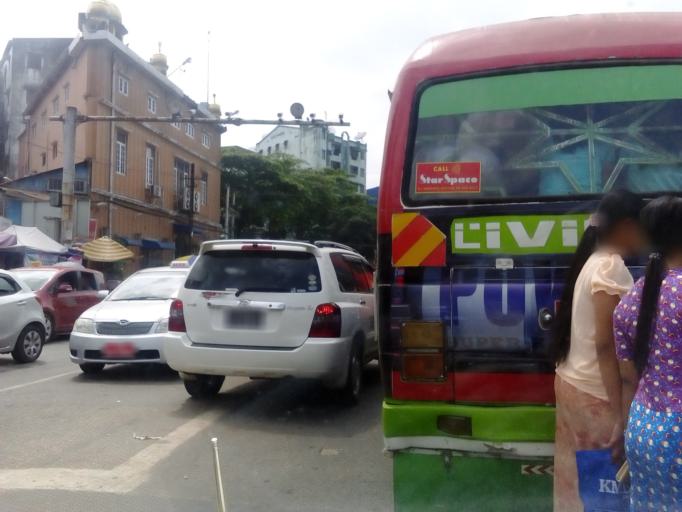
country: MM
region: Yangon
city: Yangon
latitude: 16.7925
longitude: 96.1738
